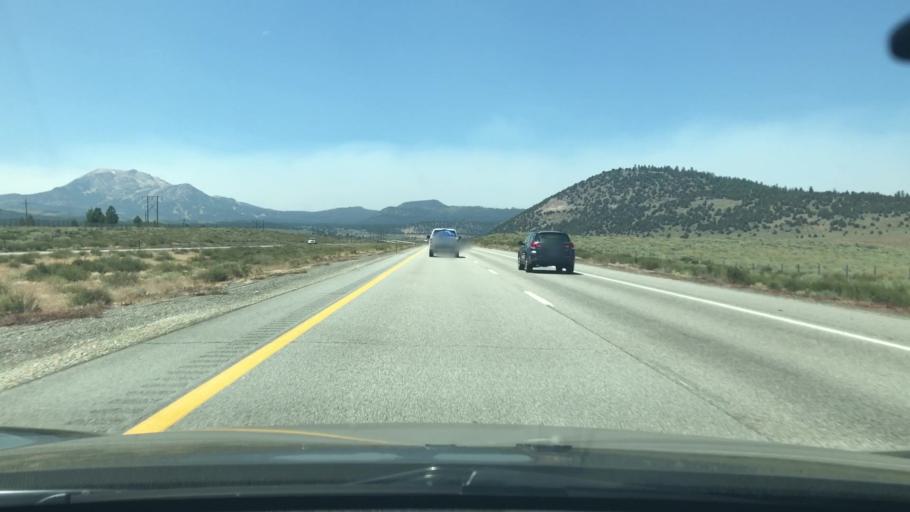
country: US
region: California
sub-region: Mono County
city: Mammoth Lakes
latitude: 37.6320
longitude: -118.8718
